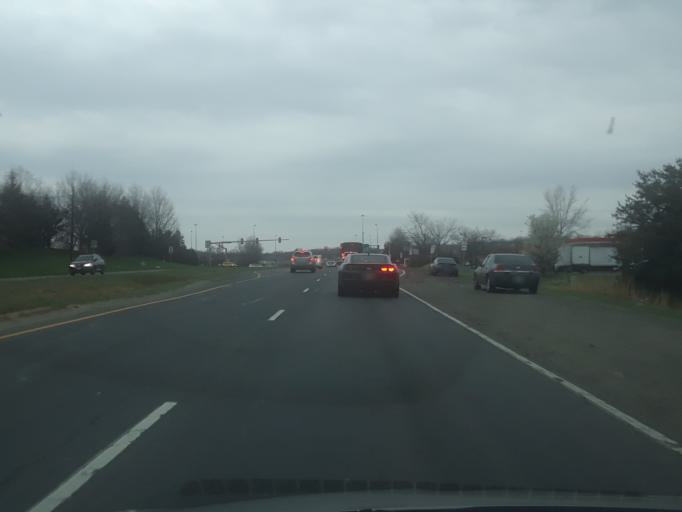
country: US
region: Virginia
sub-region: Loudoun County
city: Sterling
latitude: 38.9791
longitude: -77.4371
